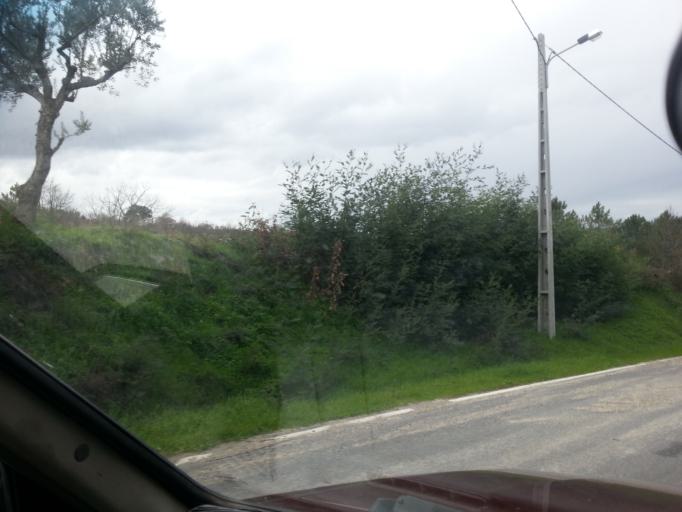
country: PT
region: Guarda
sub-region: Fornos de Algodres
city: Fornos de Algodres
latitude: 40.5770
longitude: -7.4699
